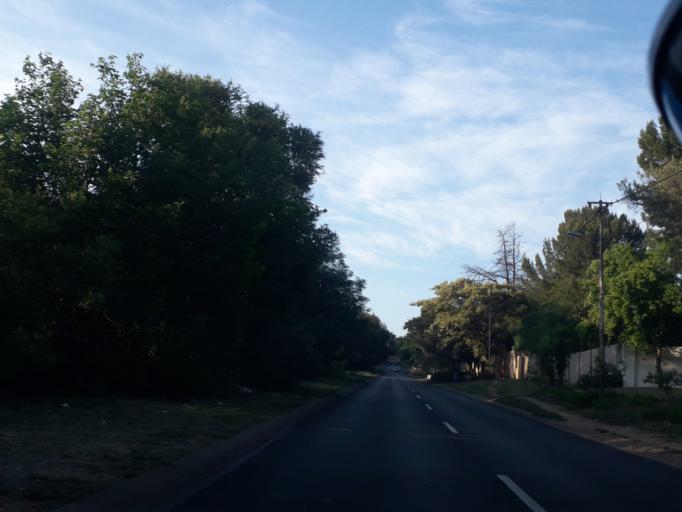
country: ZA
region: Gauteng
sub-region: City of Johannesburg Metropolitan Municipality
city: Diepsloot
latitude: -26.0617
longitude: 28.0019
